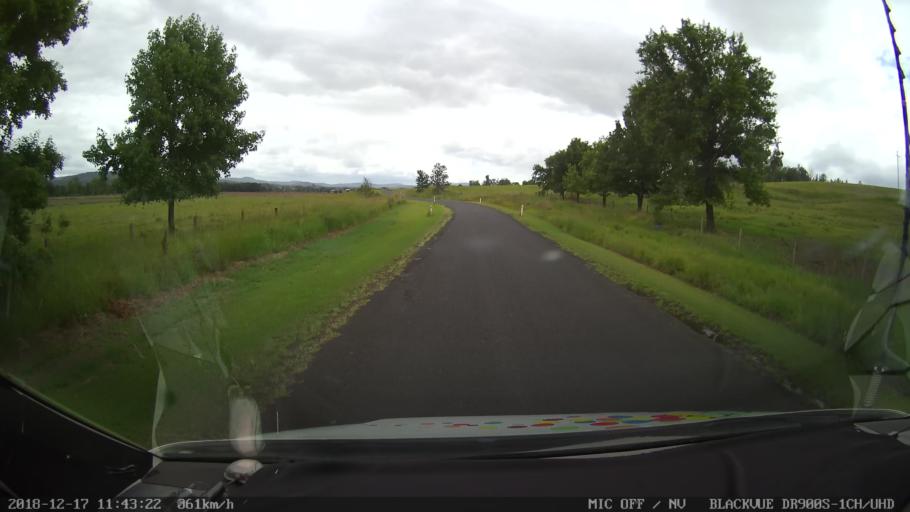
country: AU
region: New South Wales
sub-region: Kyogle
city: Kyogle
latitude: -28.6606
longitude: 152.5929
